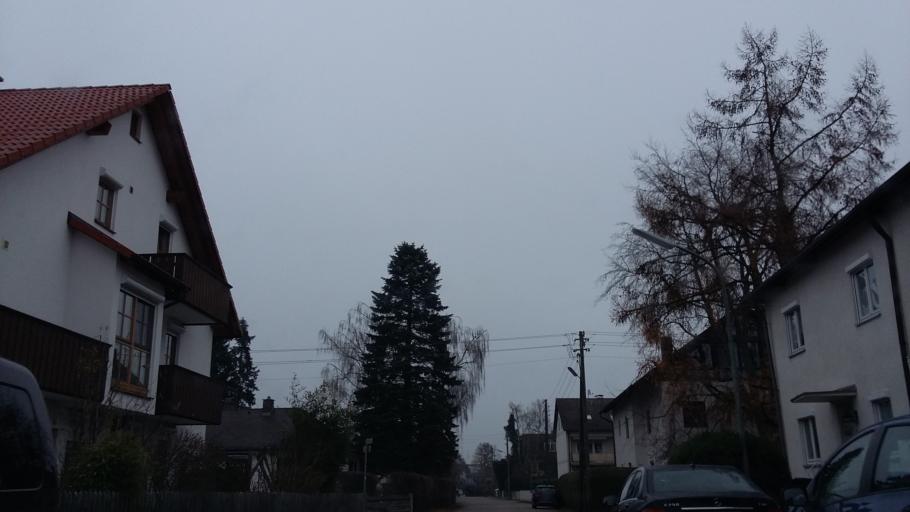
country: DE
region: Bavaria
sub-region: Upper Bavaria
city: Olching
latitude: 48.2118
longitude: 11.3415
